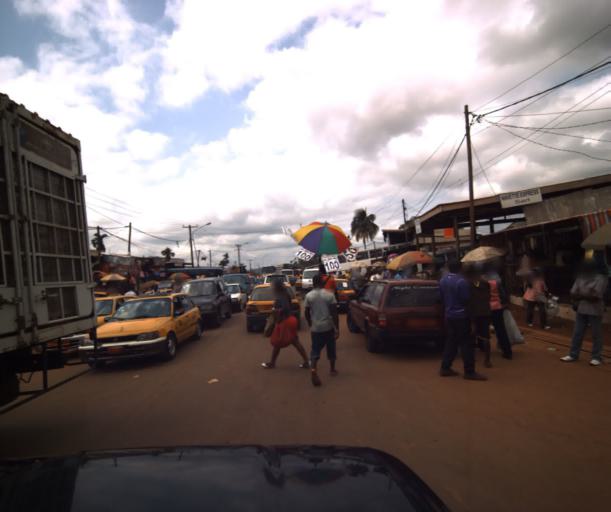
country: CM
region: Centre
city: Yaounde
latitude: 3.8237
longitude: 11.5161
